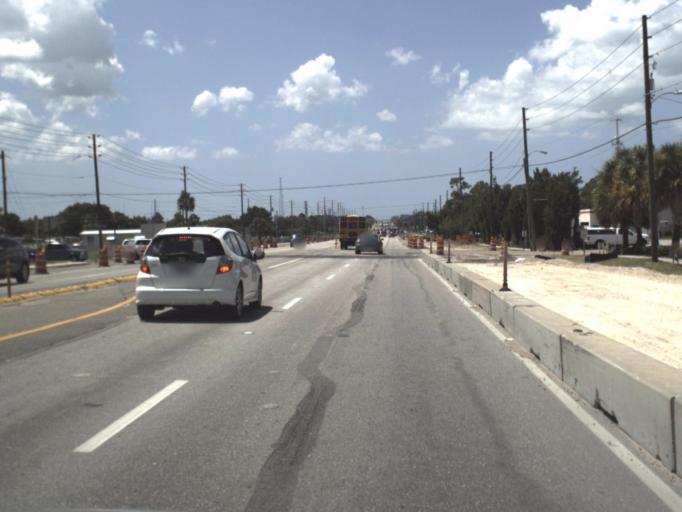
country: US
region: Florida
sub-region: Pinellas County
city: Largo
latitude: 27.8947
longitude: -82.7732
